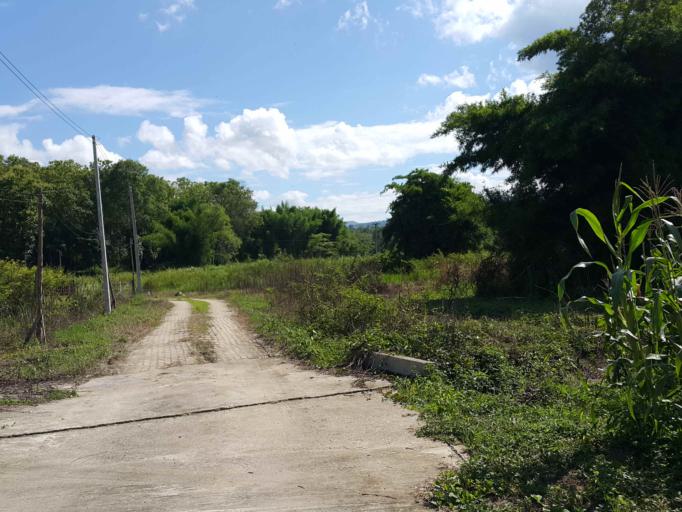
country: TH
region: Chiang Mai
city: Mae Taeng
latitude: 18.9684
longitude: 98.9101
